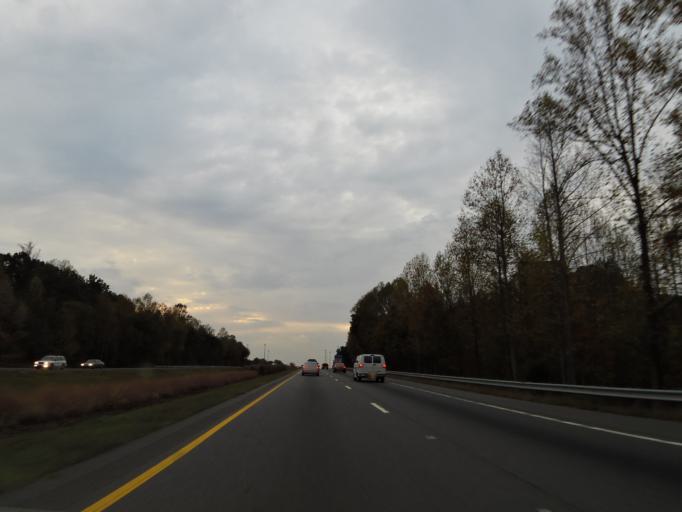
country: US
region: North Carolina
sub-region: Burke County
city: Hildebran
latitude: 35.7056
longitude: -81.4150
